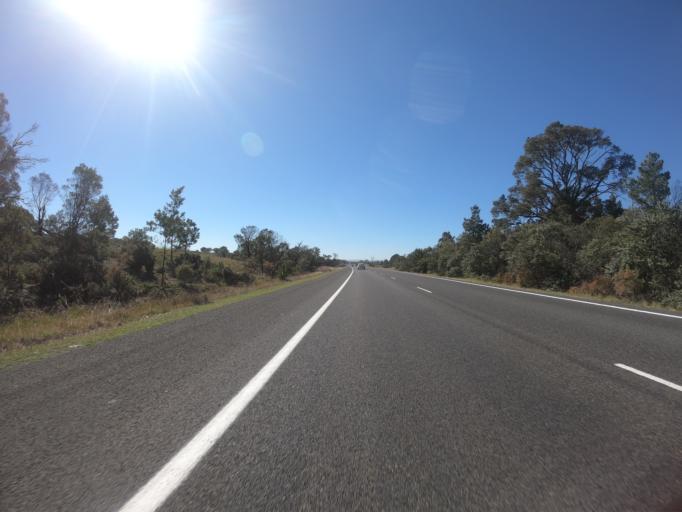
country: AU
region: New South Wales
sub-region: Goulburn Mulwaree
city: Goulburn
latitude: -34.8273
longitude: 149.5938
